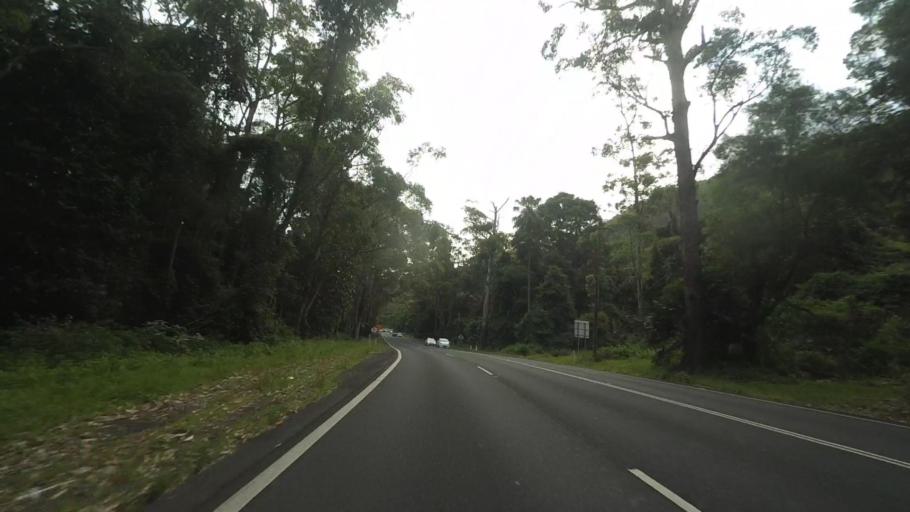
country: AU
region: New South Wales
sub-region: Wollongong
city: Bulli
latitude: -34.3188
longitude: 150.8972
